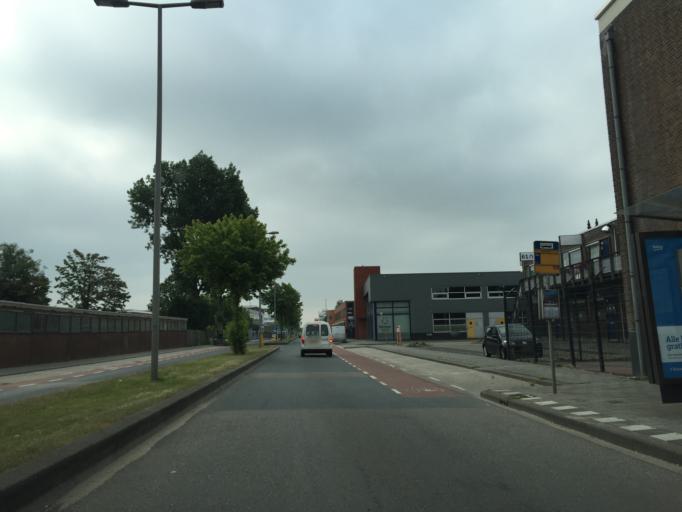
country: NL
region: South Holland
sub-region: Gemeente Schiedam
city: Schiedam
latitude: 51.9301
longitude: 4.4184
